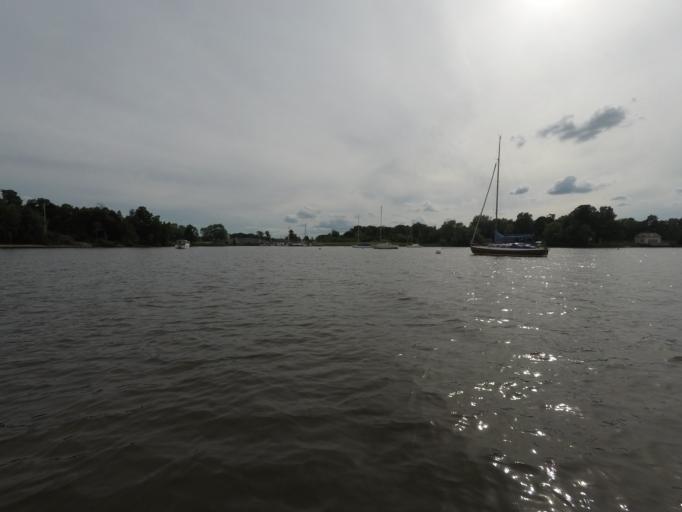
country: SE
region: Soedermanland
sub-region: Eskilstuna Kommun
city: Torshalla
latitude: 59.4532
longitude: 16.4331
